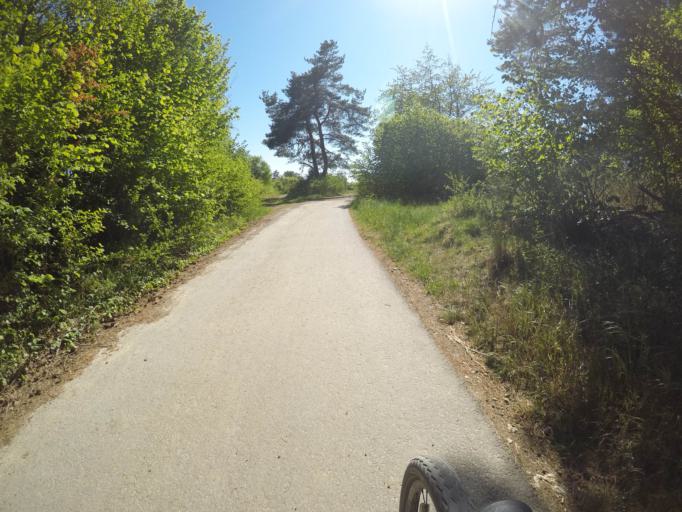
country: DE
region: Baden-Wuerttemberg
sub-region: Karlsruhe Region
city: Heimsheim
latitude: 48.8208
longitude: 8.8759
